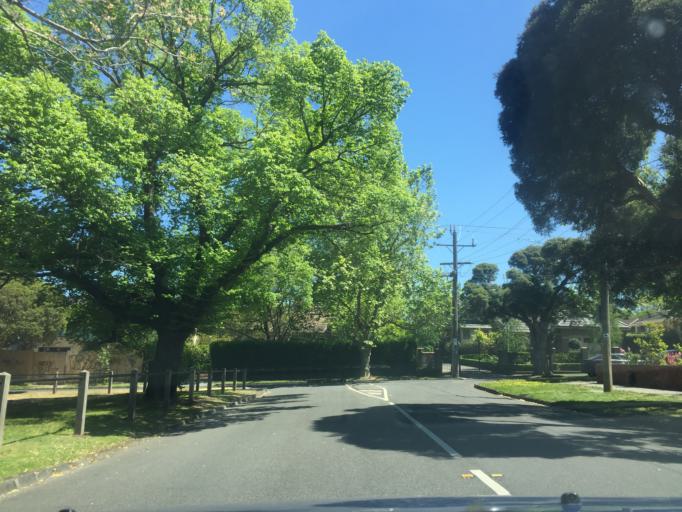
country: AU
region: Victoria
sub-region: Boroondara
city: Canterbury
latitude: -37.8215
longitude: 145.0872
